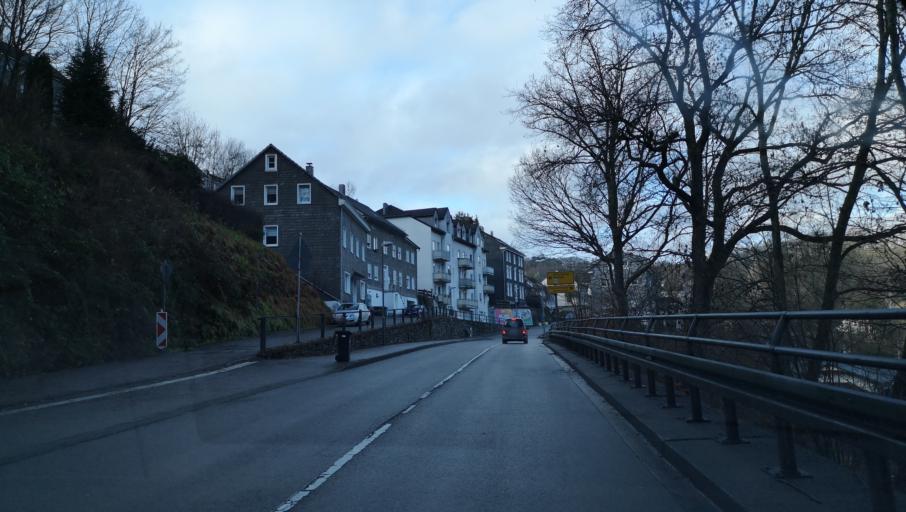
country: DE
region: North Rhine-Westphalia
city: Radevormwald
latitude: 51.2200
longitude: 7.3118
